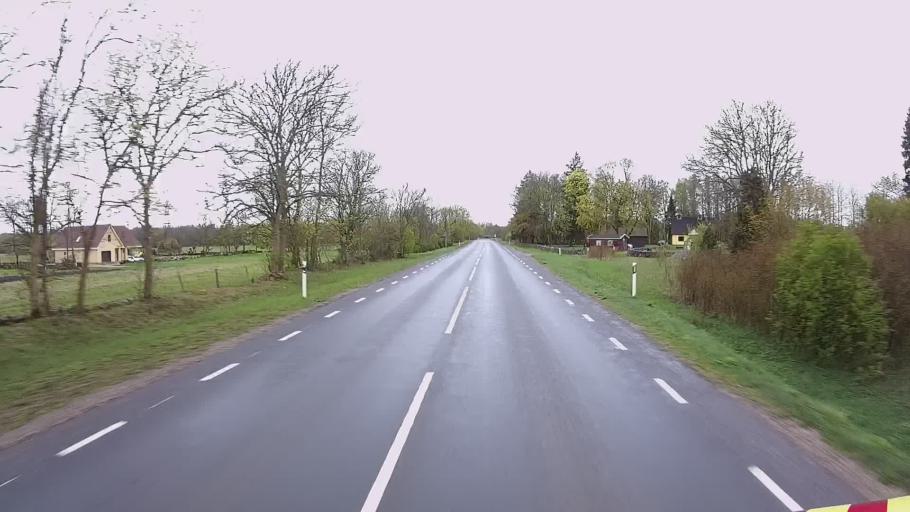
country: EE
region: Saare
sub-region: Kuressaare linn
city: Kuressaare
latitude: 58.2965
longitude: 22.5415
